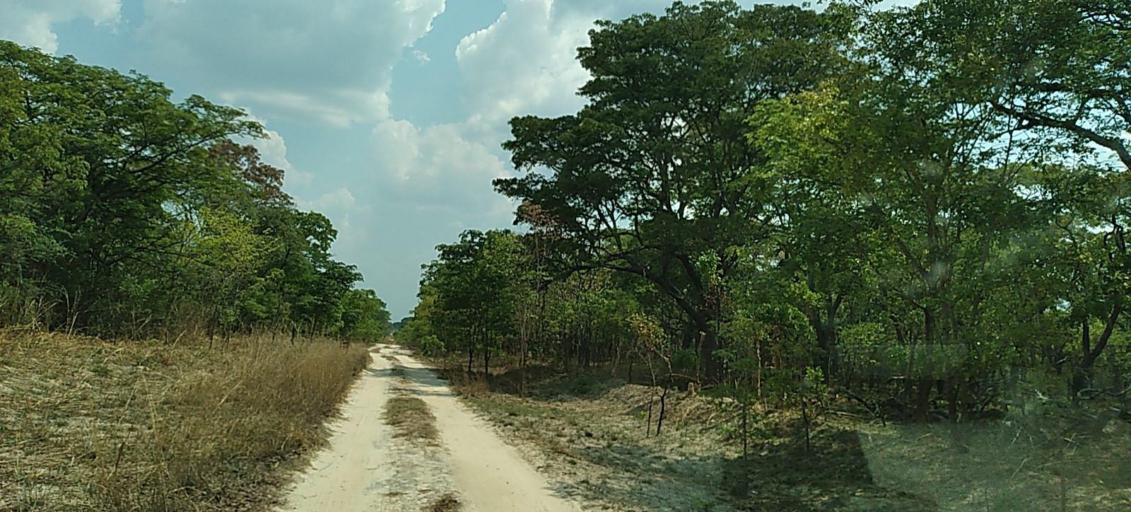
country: ZM
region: Copperbelt
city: Mpongwe
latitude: -13.8261
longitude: 27.9417
